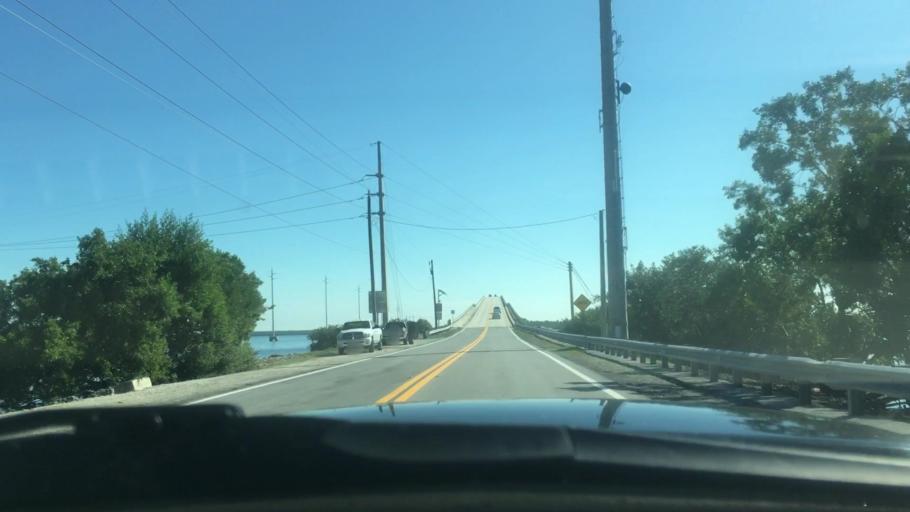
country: US
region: Florida
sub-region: Monroe County
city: North Key Largo
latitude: 25.2894
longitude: -80.3736
